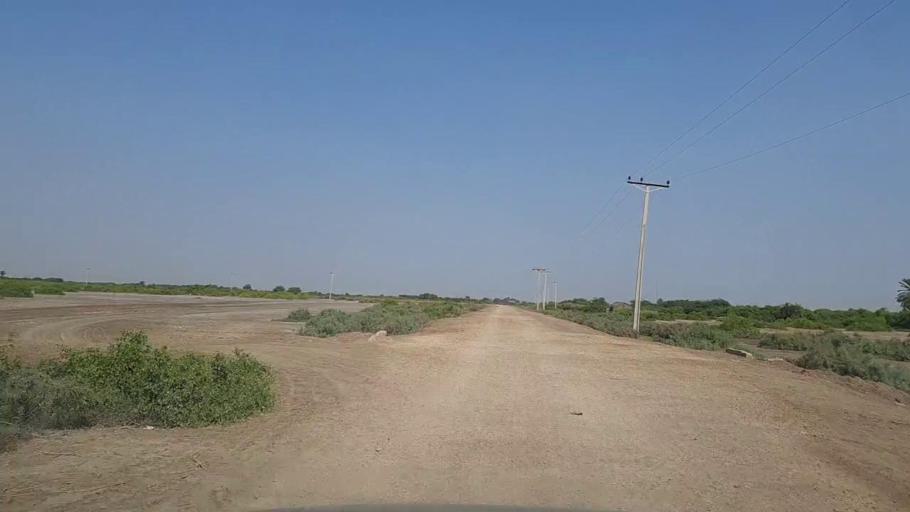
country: PK
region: Sindh
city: Thatta
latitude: 24.6053
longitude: 67.9544
